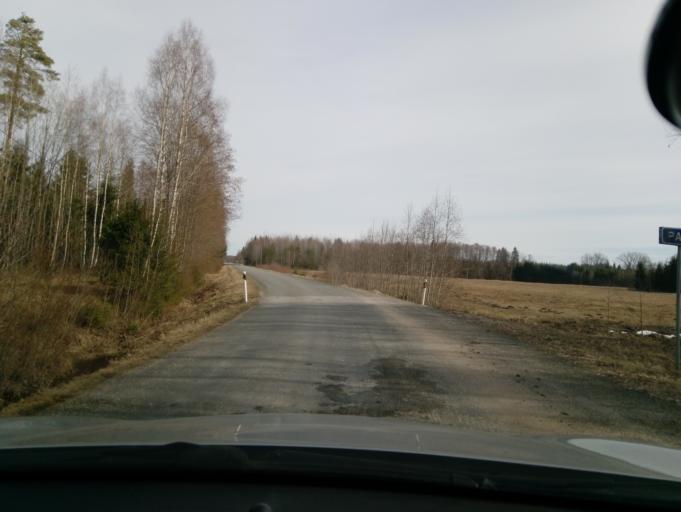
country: EE
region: Jaervamaa
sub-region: Tueri vald
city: Tueri
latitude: 58.8506
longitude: 25.3785
